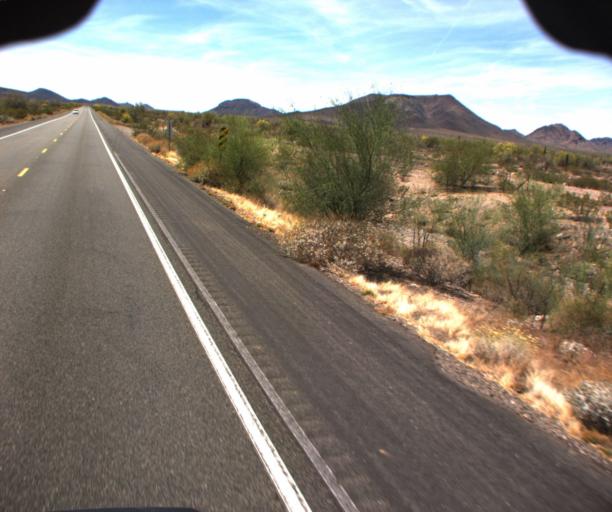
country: US
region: Arizona
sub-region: La Paz County
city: Quartzsite
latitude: 33.6700
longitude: -113.9841
